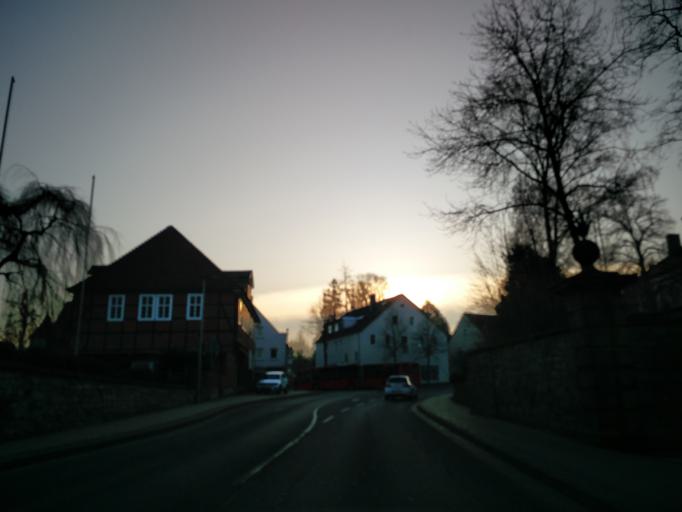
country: DE
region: North Rhine-Westphalia
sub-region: Regierungsbezirk Detmold
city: Buren
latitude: 51.5557
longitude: 8.5590
